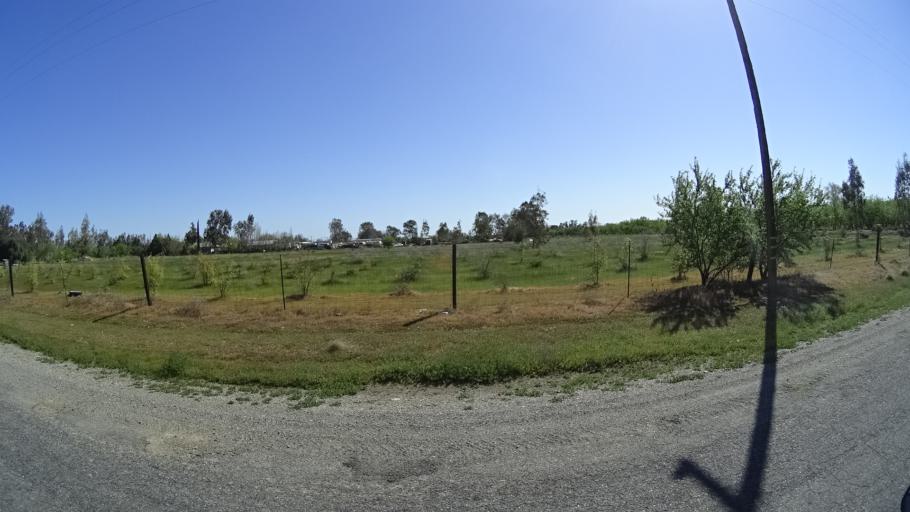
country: US
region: California
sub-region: Glenn County
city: Orland
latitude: 39.7137
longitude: -122.2114
